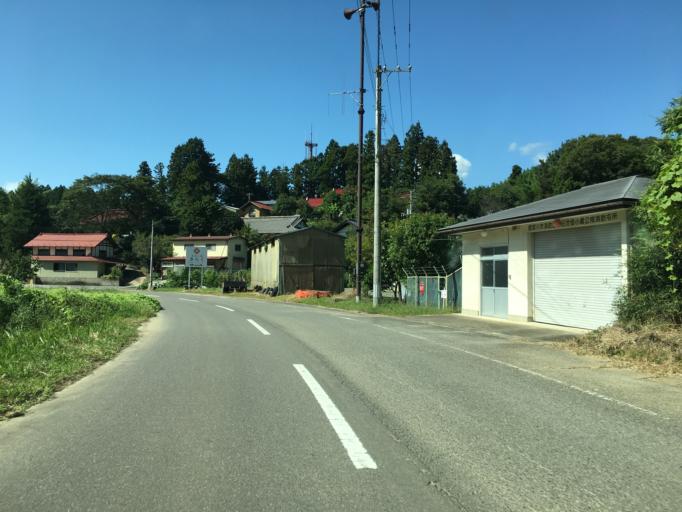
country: JP
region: Fukushima
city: Sukagawa
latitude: 37.2803
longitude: 140.4570
